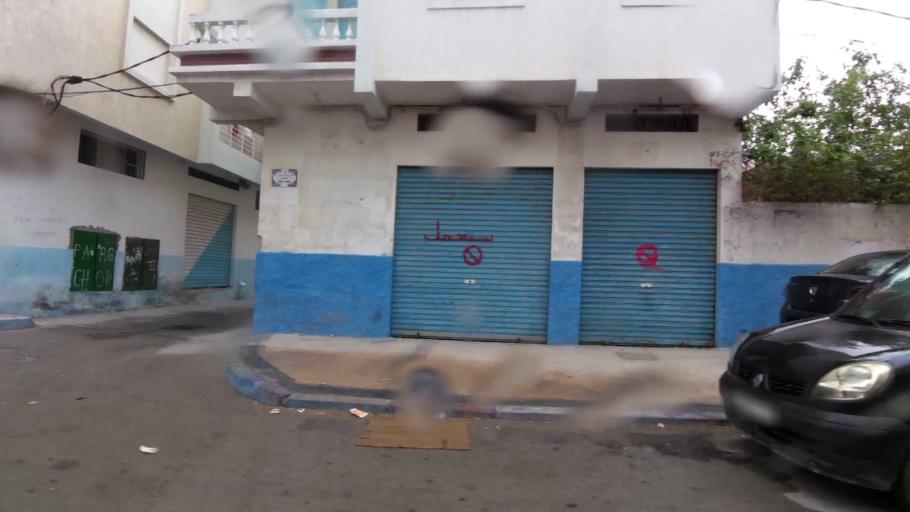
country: MA
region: Tanger-Tetouan
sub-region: Tetouan
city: Martil
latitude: 35.6230
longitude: -5.2787
